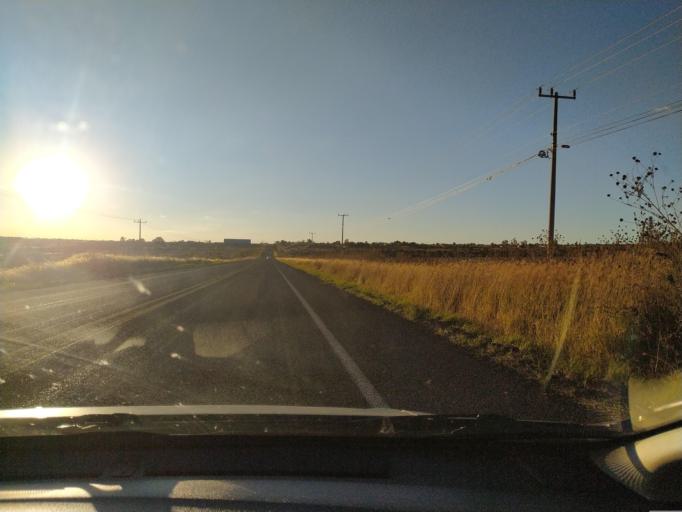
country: MX
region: Jalisco
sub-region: San Julian
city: Colonia Veintitres de Mayo
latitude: 21.0108
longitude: -102.2231
